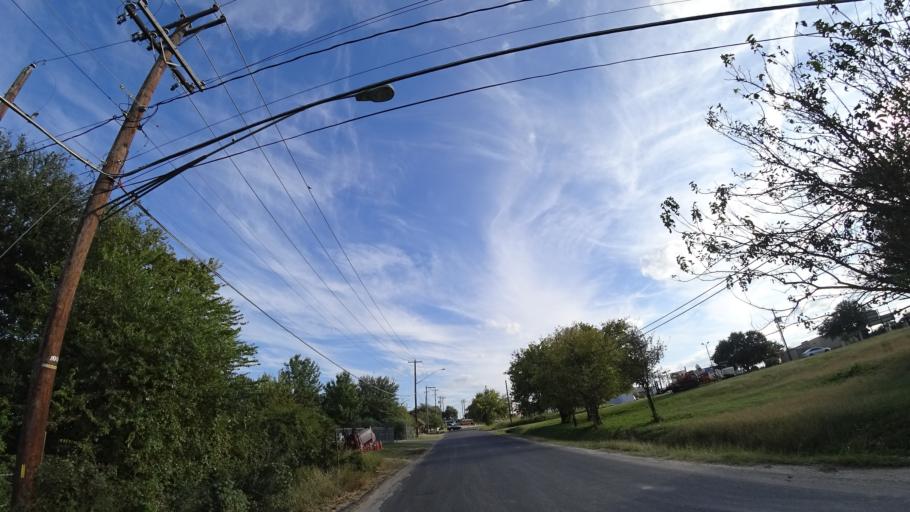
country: US
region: Texas
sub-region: Travis County
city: Onion Creek
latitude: 30.1926
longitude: -97.7716
